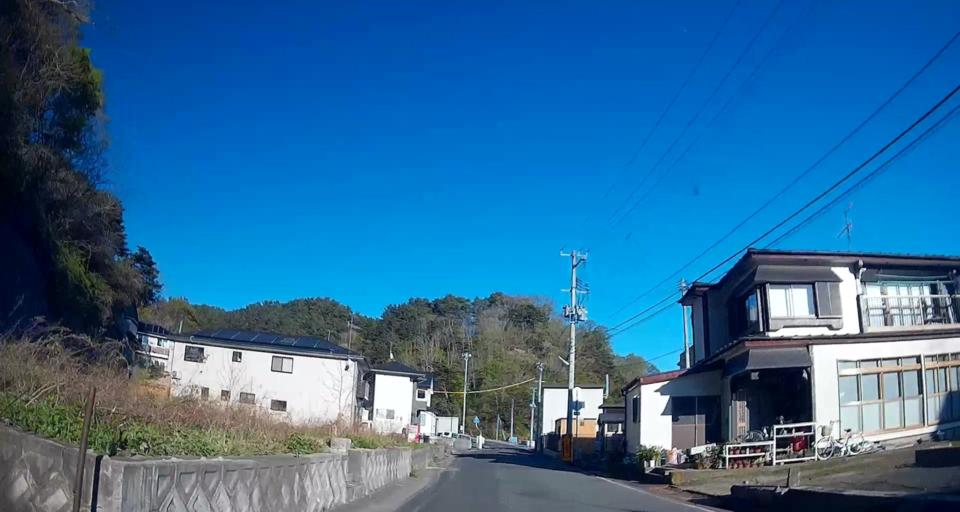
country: JP
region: Iwate
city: Miyako
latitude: 39.6453
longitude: 141.9739
